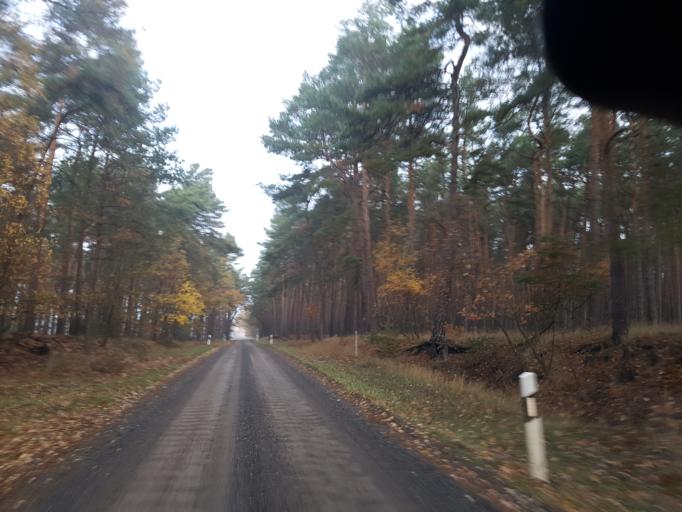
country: DE
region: Saxony-Anhalt
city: Abtsdorf
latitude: 51.9154
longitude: 12.7455
